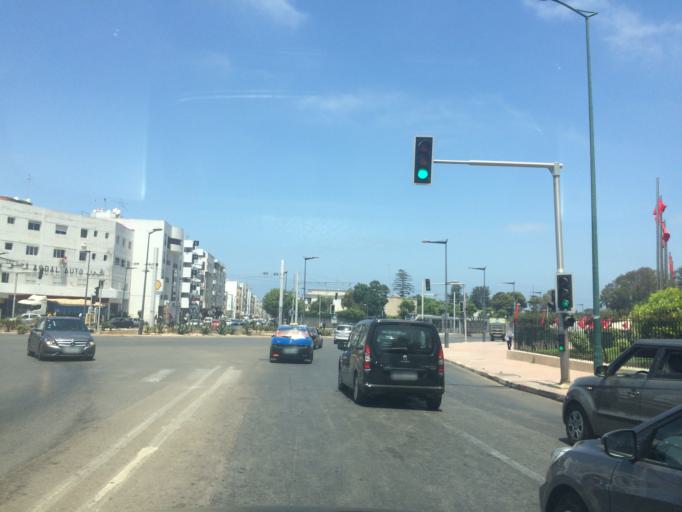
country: MA
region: Rabat-Sale-Zemmour-Zaer
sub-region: Rabat
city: Rabat
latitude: 33.9985
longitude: -6.8438
